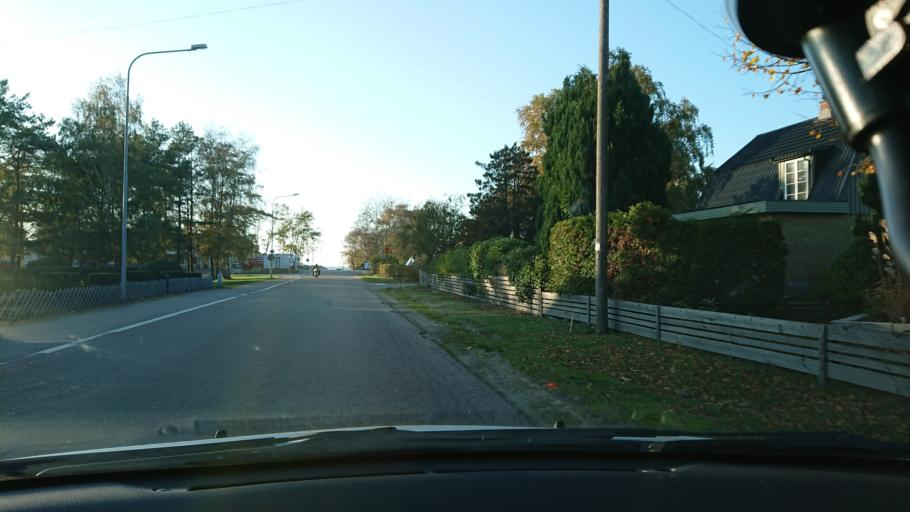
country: SE
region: Halland
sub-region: Laholms Kommun
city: Mellbystrand
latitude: 56.4607
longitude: 12.9233
